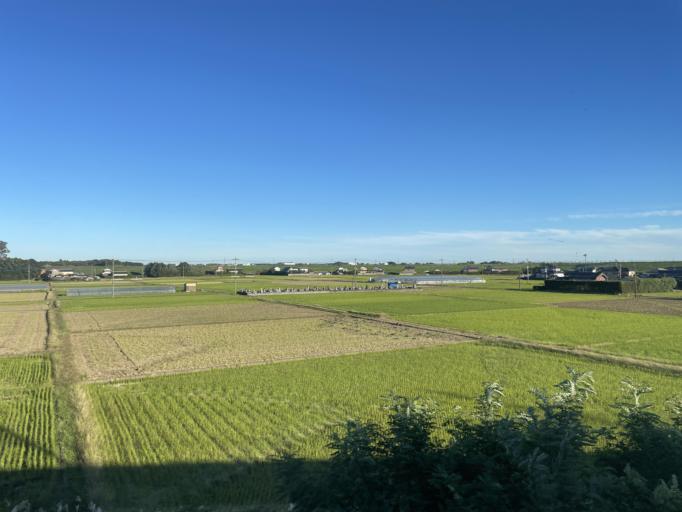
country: JP
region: Ibaraki
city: Koga
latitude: 36.1669
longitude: 139.6849
